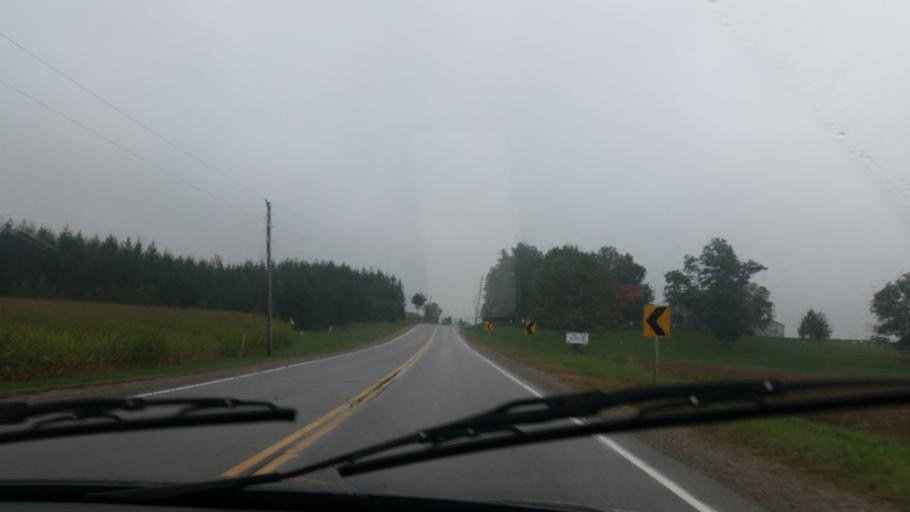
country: CA
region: Ontario
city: London
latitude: 43.0724
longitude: -81.3386
